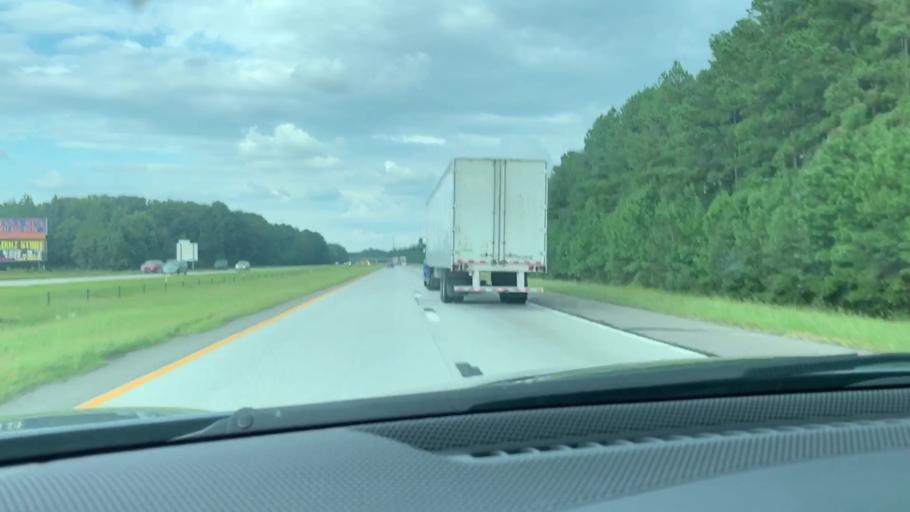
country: US
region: South Carolina
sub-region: Dorchester County
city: Saint George
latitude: 33.2861
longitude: -80.5618
